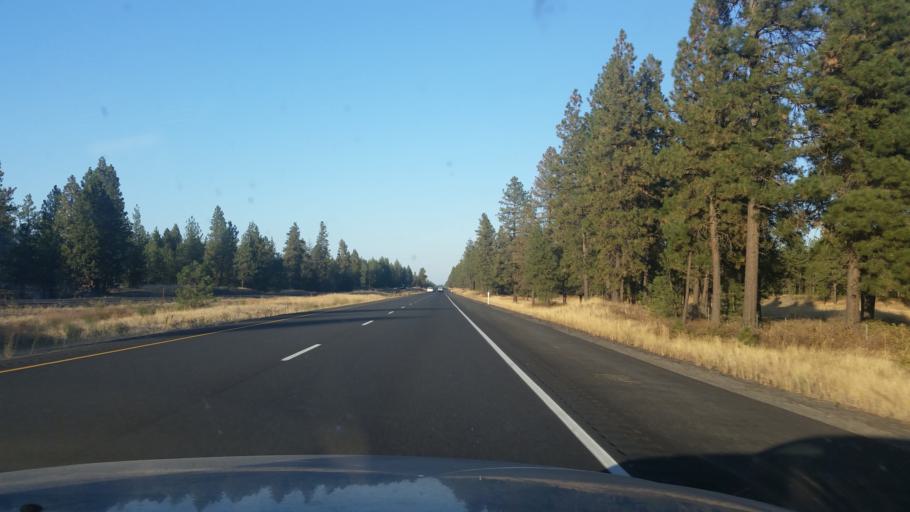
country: US
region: Washington
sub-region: Spokane County
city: Medical Lake
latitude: 47.4720
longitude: -117.7378
